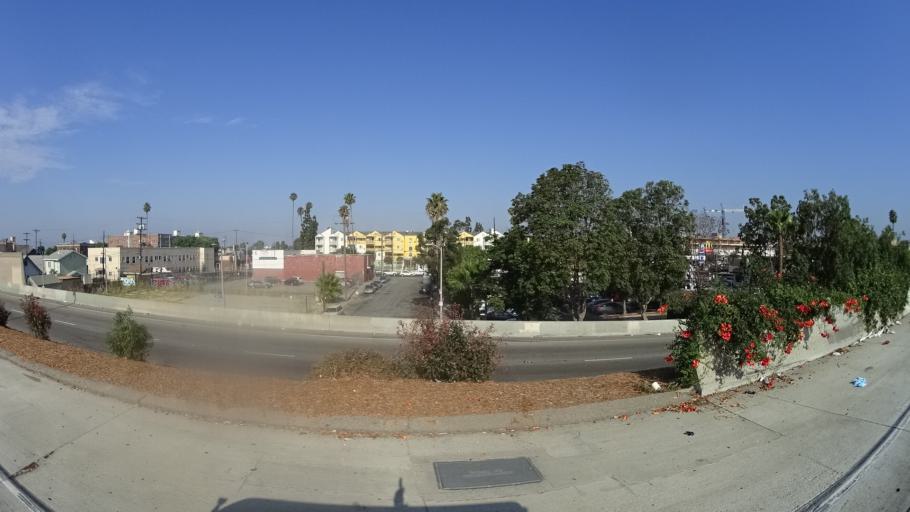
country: US
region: California
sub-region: Los Angeles County
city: Florence-Graham
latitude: 34.0103
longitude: -118.2814
